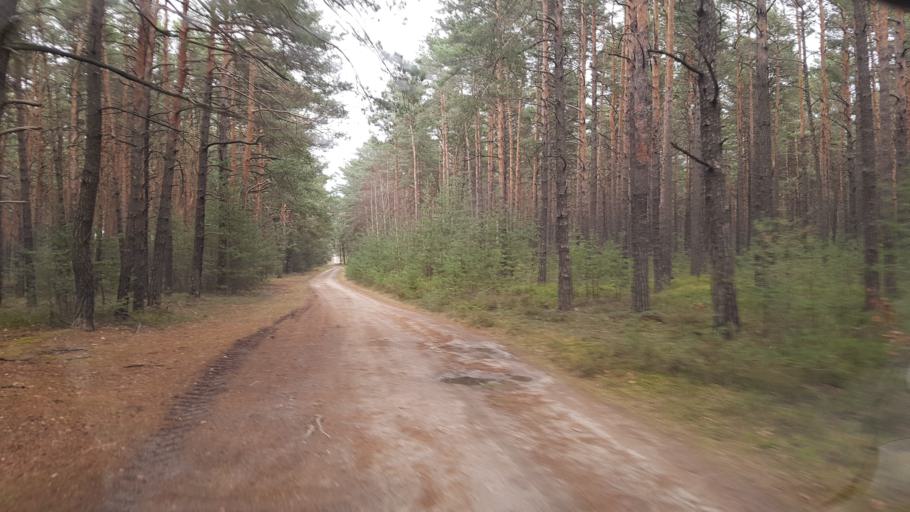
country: DE
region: Brandenburg
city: Sallgast
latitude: 51.6151
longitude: 13.7901
